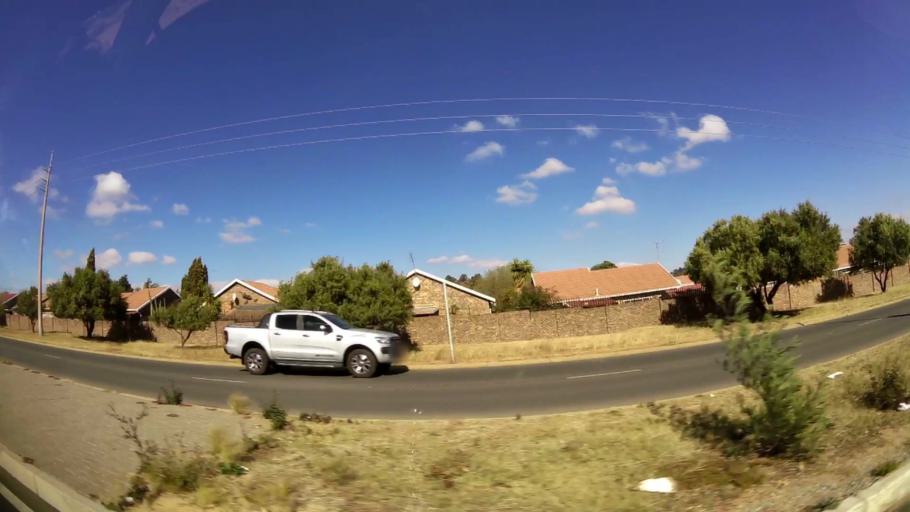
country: ZA
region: Gauteng
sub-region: West Rand District Municipality
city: Krugersdorp
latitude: -26.0833
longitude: 27.8048
